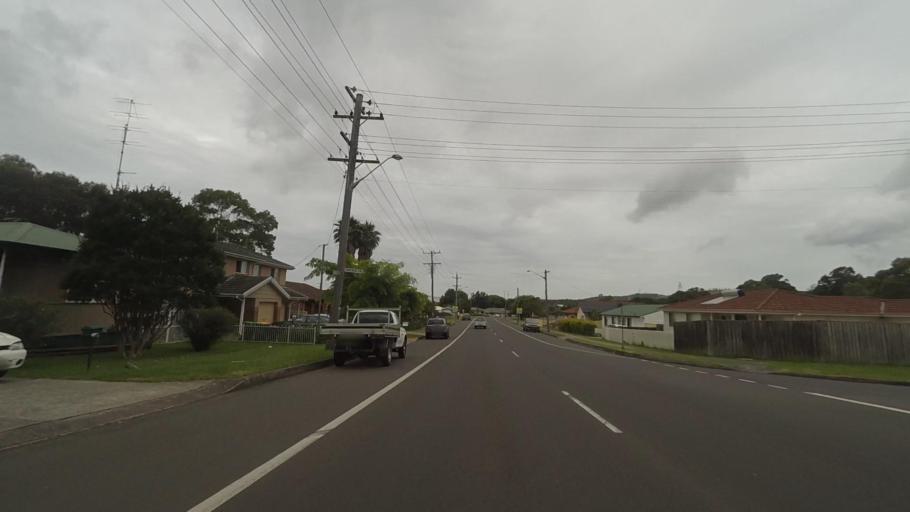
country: AU
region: New South Wales
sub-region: Wollongong
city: Cordeaux Heights
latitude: -34.4583
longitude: 150.8339
